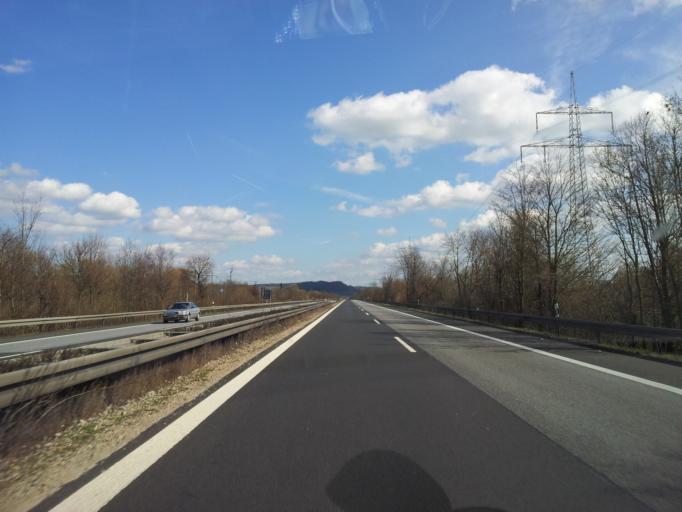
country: DE
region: Bavaria
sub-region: Regierungsbezirk Unterfranken
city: Ebelsbach
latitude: 49.9749
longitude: 10.6931
